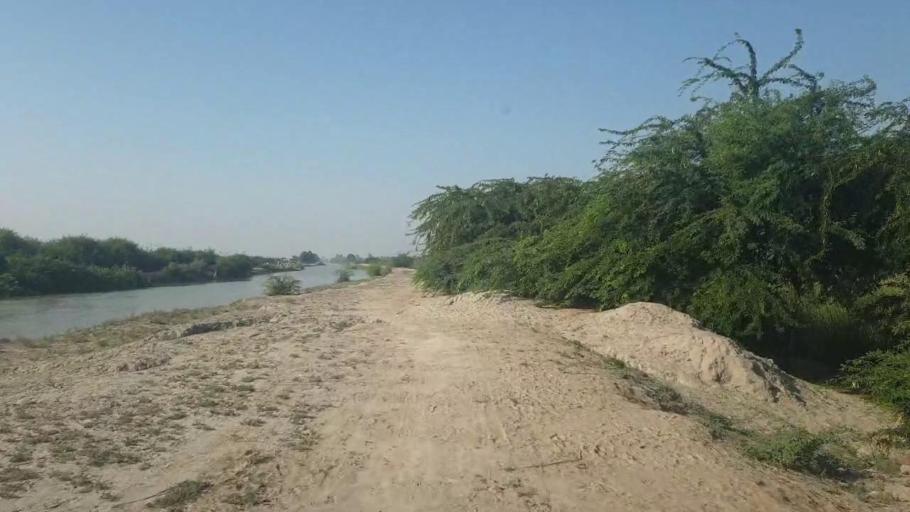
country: PK
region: Sindh
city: Badin
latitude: 24.7094
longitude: 68.8910
